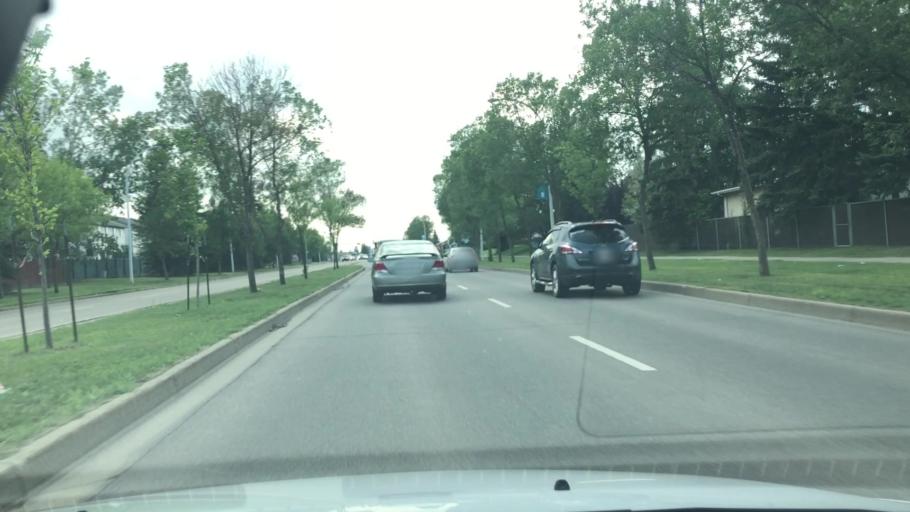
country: CA
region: Alberta
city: Edmonton
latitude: 53.6170
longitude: -113.5363
